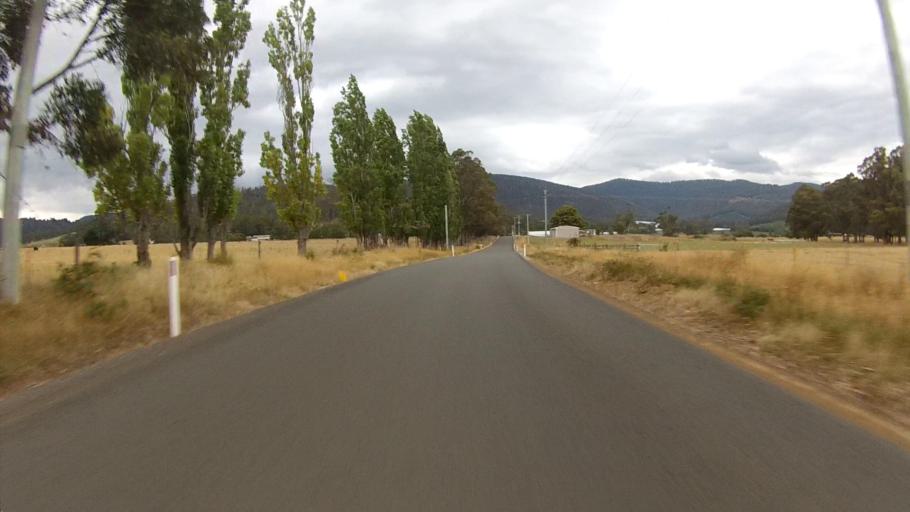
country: AU
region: Tasmania
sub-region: Huon Valley
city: Huonville
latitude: -42.9747
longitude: 147.0929
